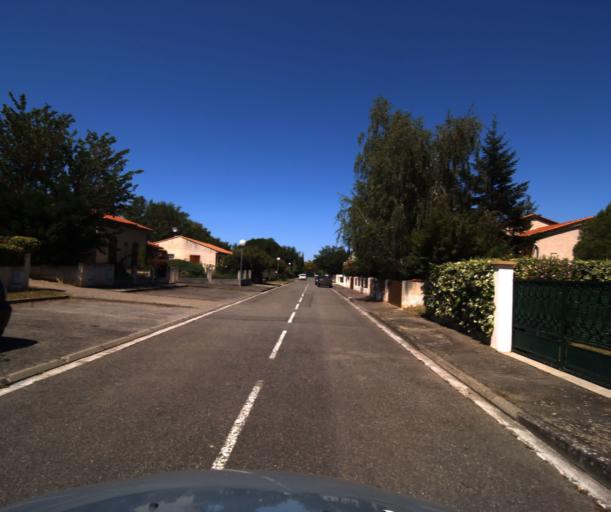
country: FR
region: Midi-Pyrenees
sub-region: Departement de la Haute-Garonne
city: Muret
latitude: 43.4538
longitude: 1.3265
